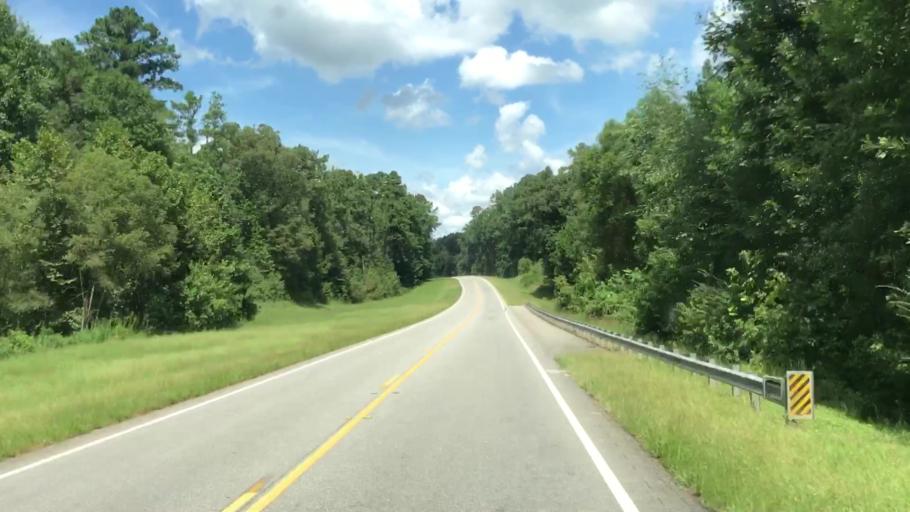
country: US
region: Georgia
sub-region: Greene County
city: Greensboro
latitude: 33.6920
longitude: -83.2761
